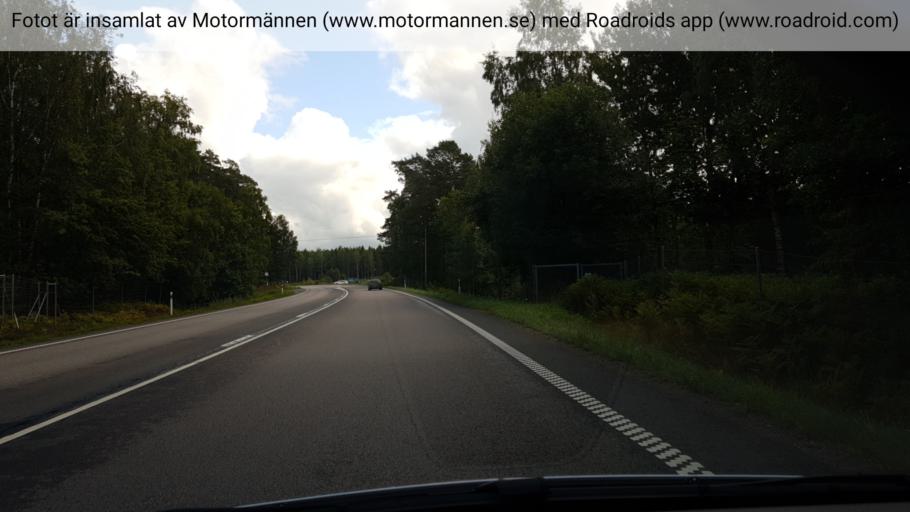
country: SE
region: Vaestra Goetaland
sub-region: Lidkopings Kommun
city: Vinninga
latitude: 58.4325
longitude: 13.2882
